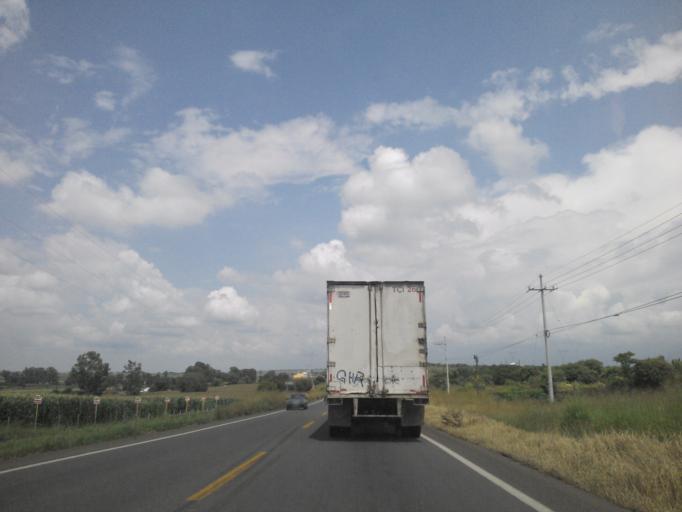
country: MX
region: Jalisco
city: Acatic
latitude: 20.7052
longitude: -102.9629
